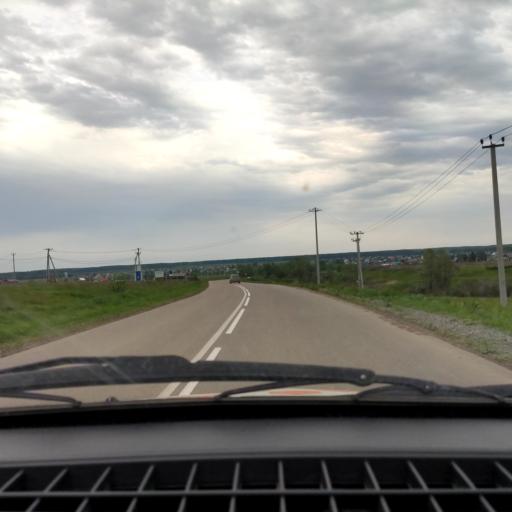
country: RU
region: Bashkortostan
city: Avdon
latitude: 54.5621
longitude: 55.7616
